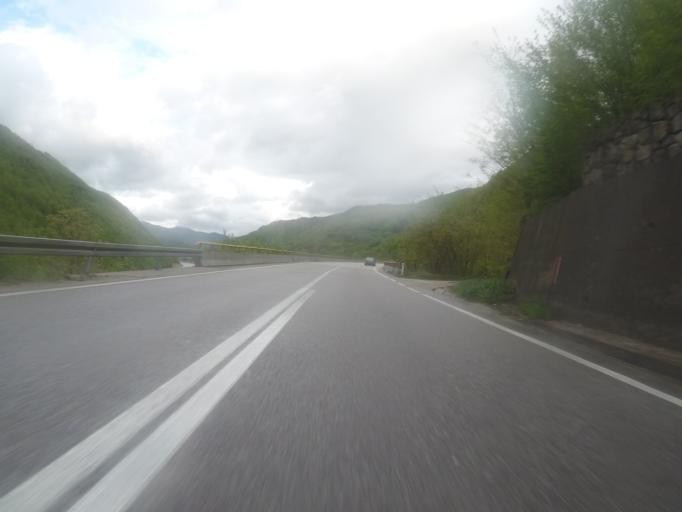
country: BA
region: Federation of Bosnia and Herzegovina
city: Jablanica
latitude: 43.6840
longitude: 17.7953
